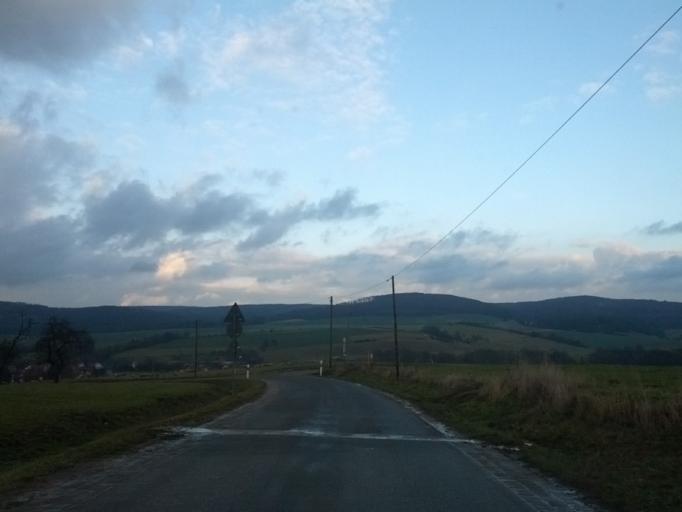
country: DE
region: Thuringia
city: Bischofroda
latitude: 51.0484
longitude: 10.3618
